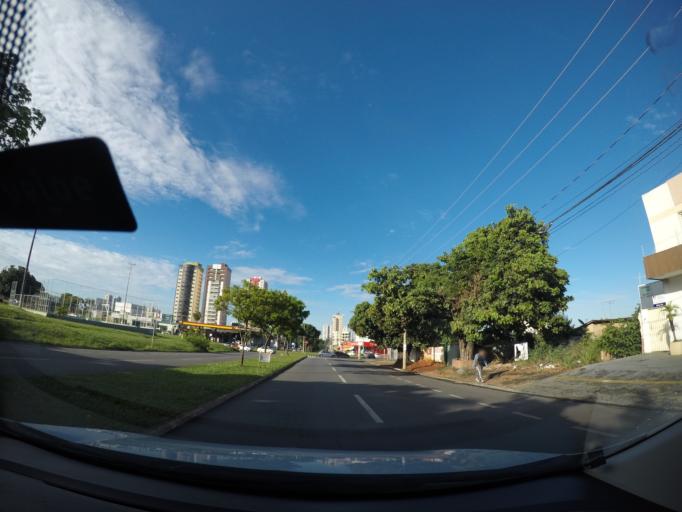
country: BR
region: Goias
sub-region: Goiania
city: Goiania
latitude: -16.7237
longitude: -49.2698
